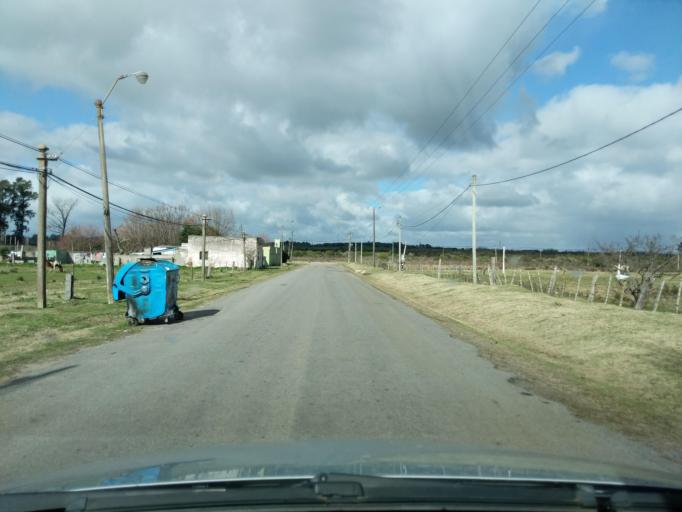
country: UY
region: Florida
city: Florida
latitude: -34.1089
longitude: -56.2221
